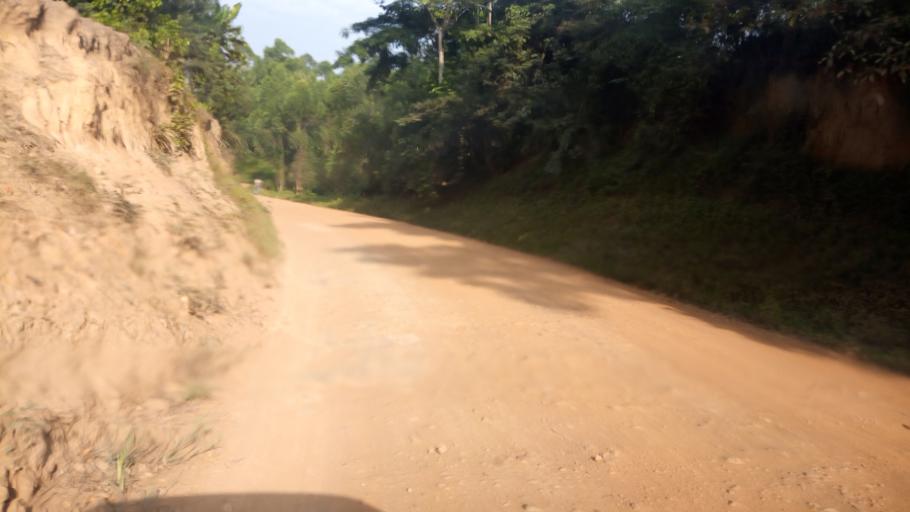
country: UG
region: Western Region
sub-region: Kanungu District
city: Ntungamo
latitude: -0.8347
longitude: 29.6721
